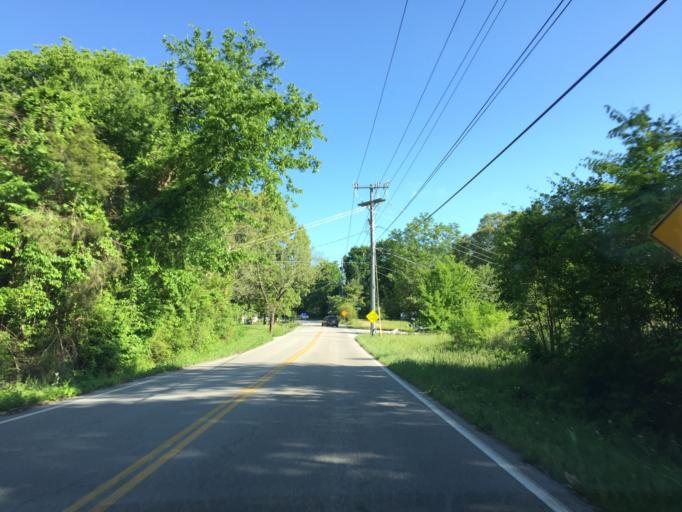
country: US
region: Tennessee
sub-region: Hamilton County
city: Harrison
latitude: 35.1226
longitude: -85.1105
